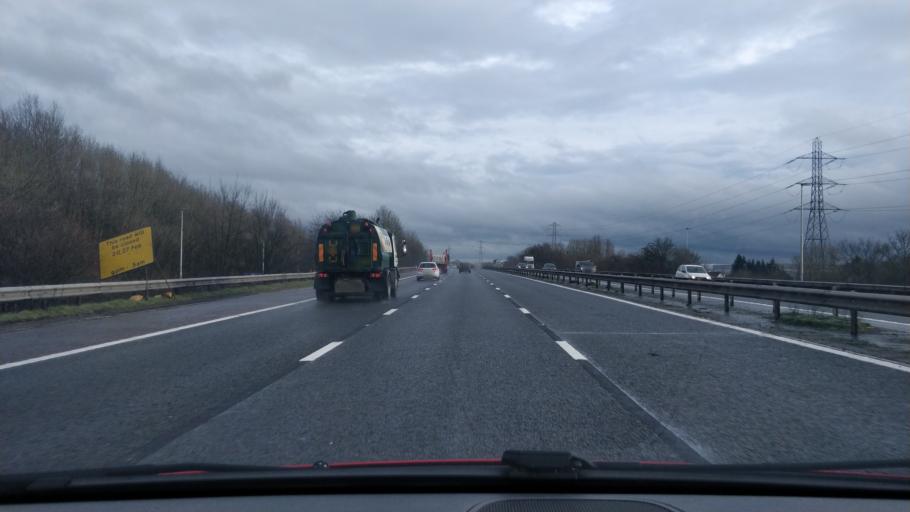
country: GB
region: England
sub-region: Knowsley
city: Kirkby
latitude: 53.4753
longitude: -2.9038
